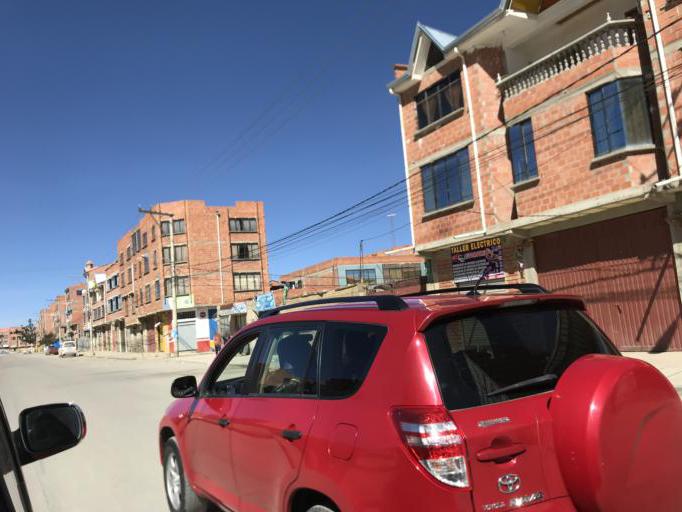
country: BO
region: La Paz
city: La Paz
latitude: -16.4862
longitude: -68.2045
